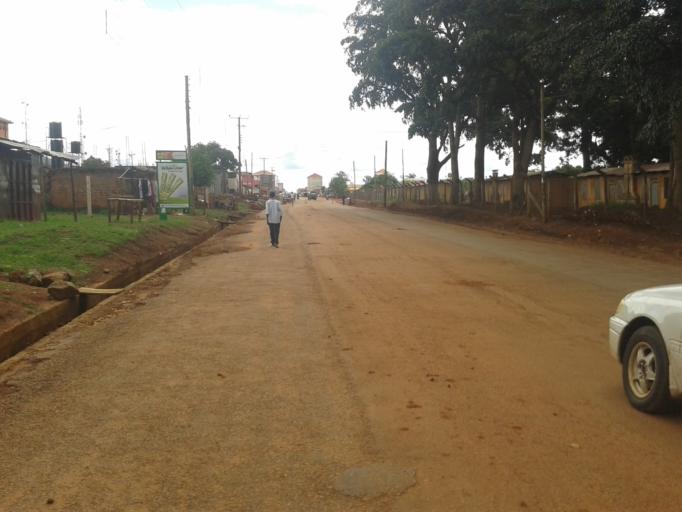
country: UG
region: Northern Region
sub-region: Gulu District
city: Gulu
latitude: 2.7707
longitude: 32.3063
